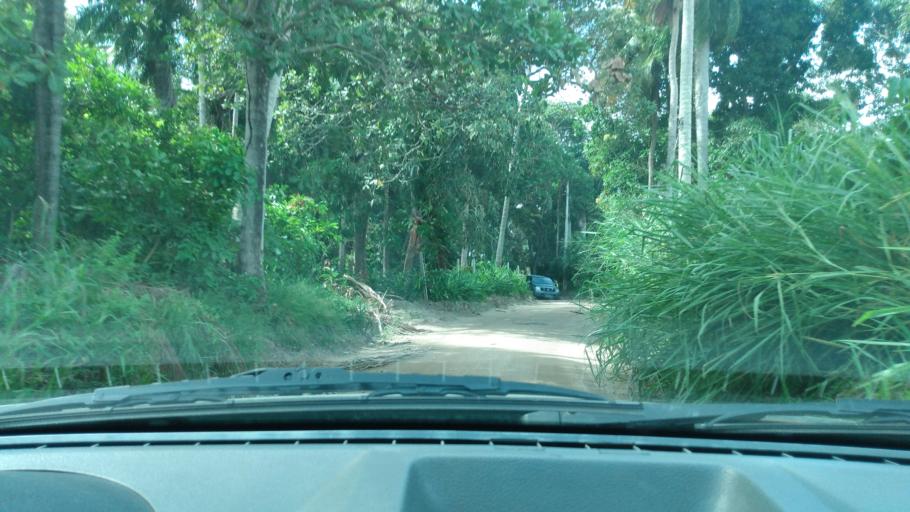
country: BR
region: Pernambuco
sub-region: Cabo De Santo Agostinho
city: Cabo
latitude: -8.3582
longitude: -34.9666
